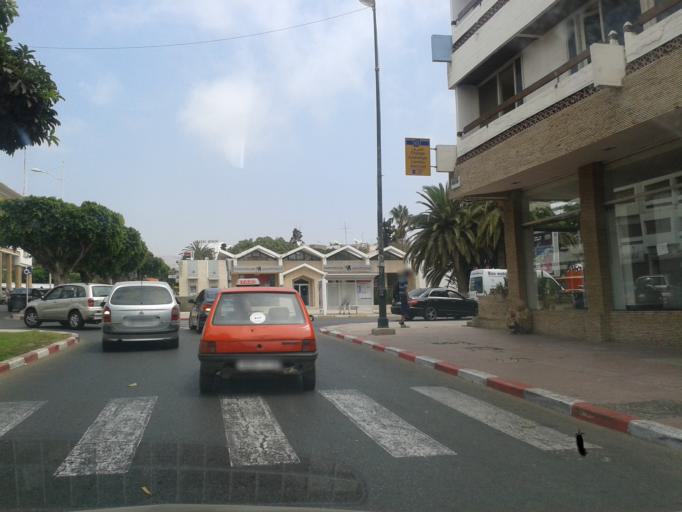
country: MA
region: Souss-Massa-Draa
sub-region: Agadir-Ida-ou-Tnan
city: Agadir
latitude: 30.4230
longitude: -9.6033
